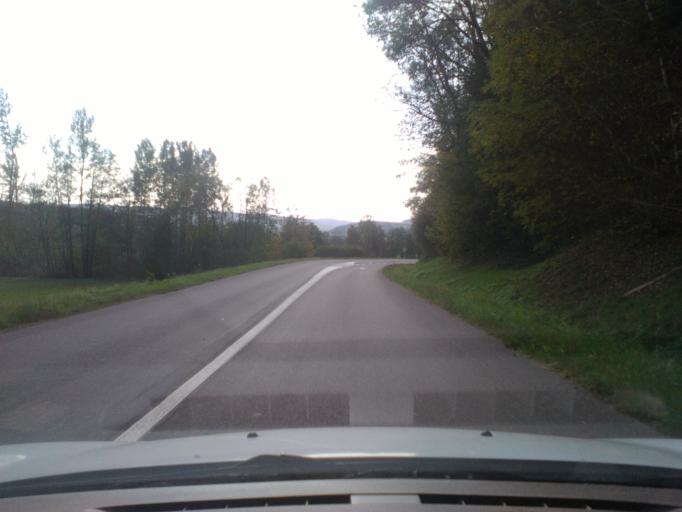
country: FR
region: Lorraine
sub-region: Departement des Vosges
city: Ban-de-Laveline
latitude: 48.2844
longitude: 7.0545
